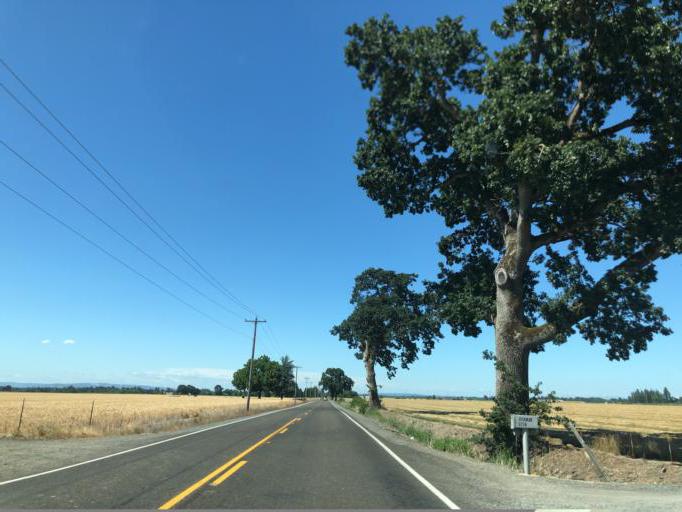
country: US
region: Oregon
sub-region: Marion County
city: Silverton
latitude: 45.0453
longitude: -122.7435
